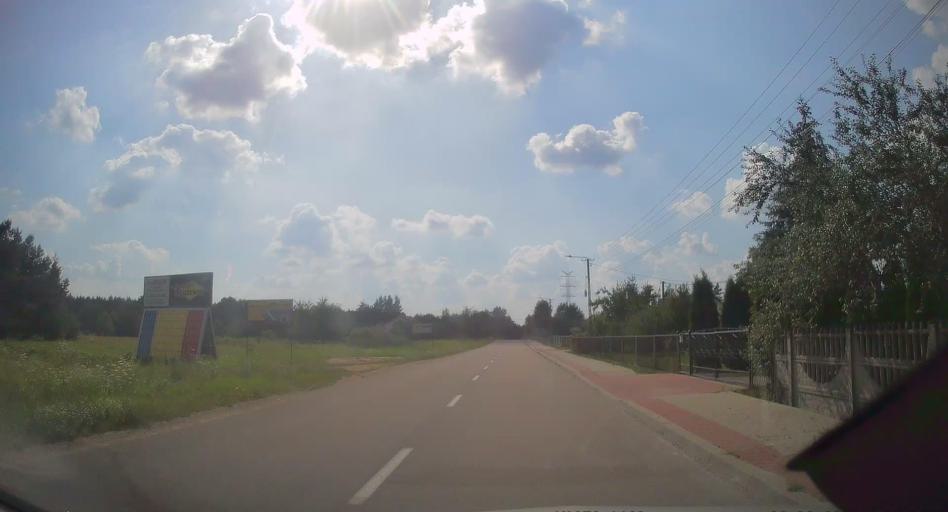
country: PL
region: Swietokrzyskie
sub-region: Powiat jedrzejowski
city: Malogoszcz
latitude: 50.8663
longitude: 20.3122
